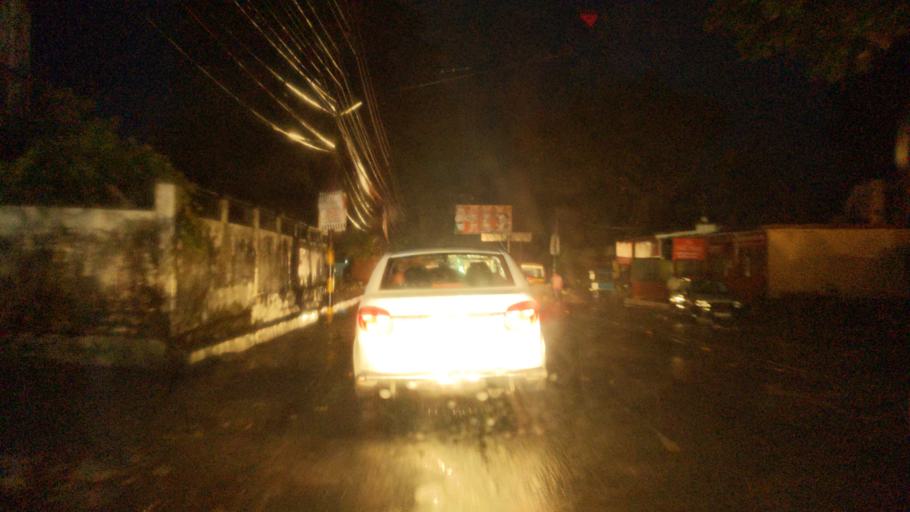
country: IN
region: Uttarakhand
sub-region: Naini Tal
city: Haldwani
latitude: 29.2735
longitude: 79.5450
